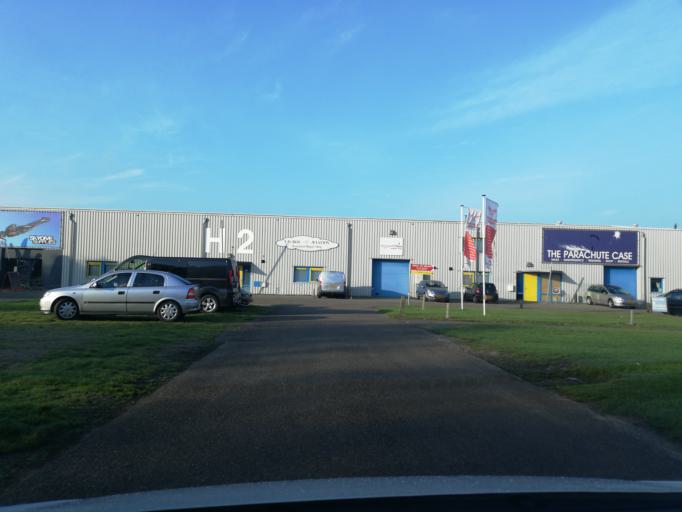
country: NL
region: Gelderland
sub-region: Gemeente Voorst
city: Twello
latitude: 52.2405
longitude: 6.0454
